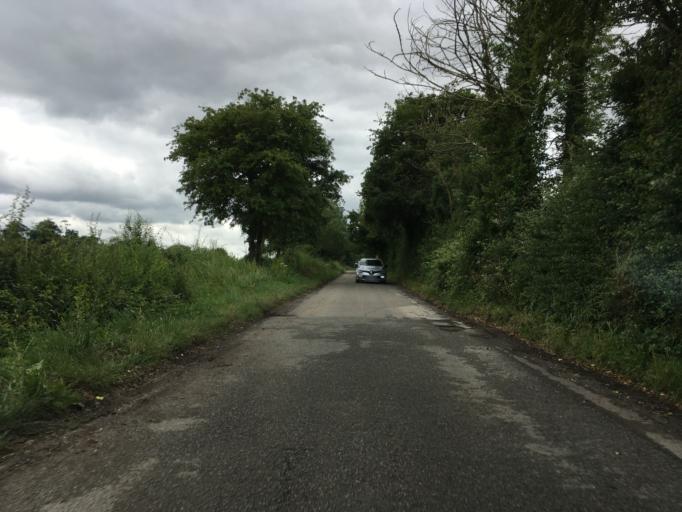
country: GB
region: England
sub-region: Gloucestershire
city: Stonehouse
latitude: 51.7910
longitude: -2.3729
